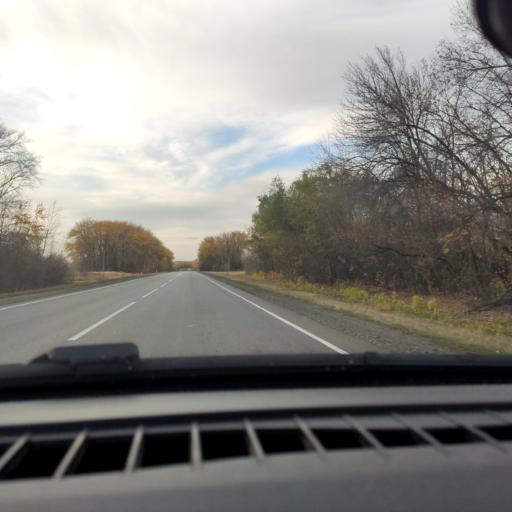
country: RU
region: Voronezj
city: Ostrogozhsk
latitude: 50.9656
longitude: 39.0135
